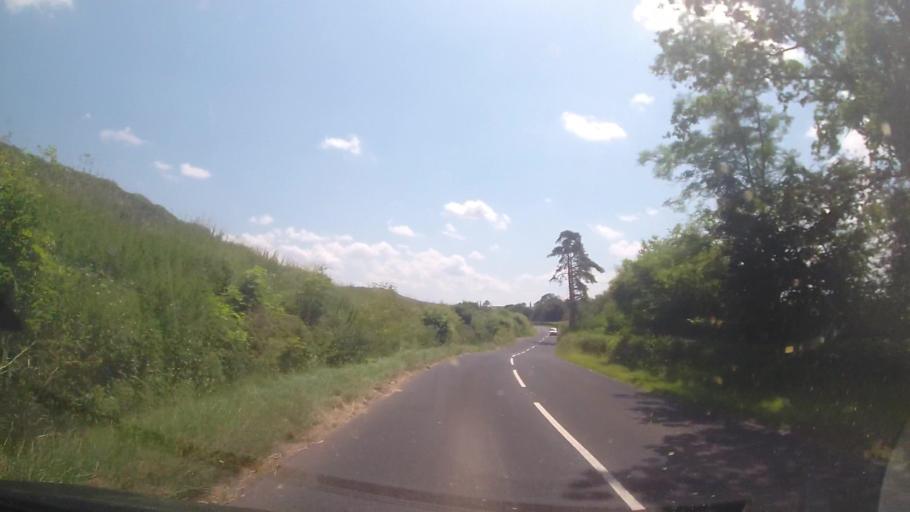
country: GB
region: England
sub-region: Herefordshire
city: Brockhampton
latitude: 52.0151
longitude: -2.6244
